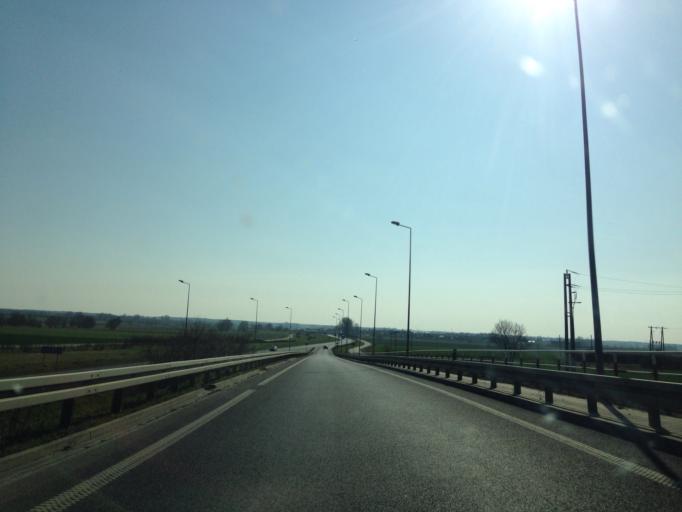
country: PL
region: Lower Silesian Voivodeship
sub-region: Powiat olesnicki
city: Olesnica
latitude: 51.2114
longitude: 17.3443
